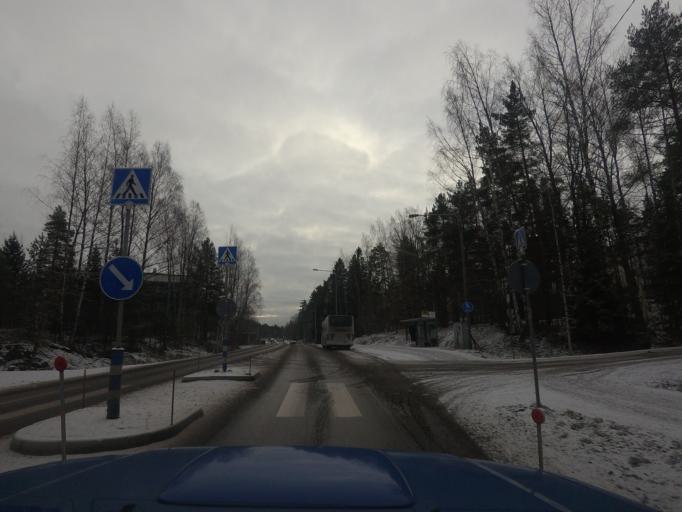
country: FI
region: Uusimaa
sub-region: Helsinki
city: Kilo
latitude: 60.2330
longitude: 24.7731
